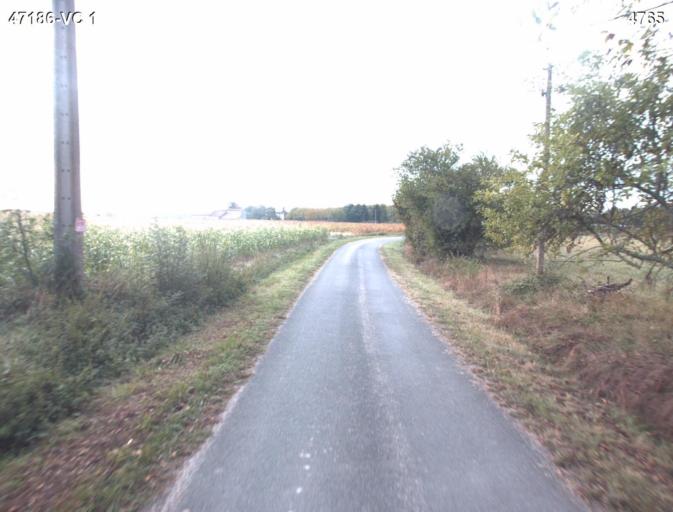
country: FR
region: Aquitaine
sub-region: Departement du Lot-et-Garonne
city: Port-Sainte-Marie
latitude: 44.2271
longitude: 0.4381
